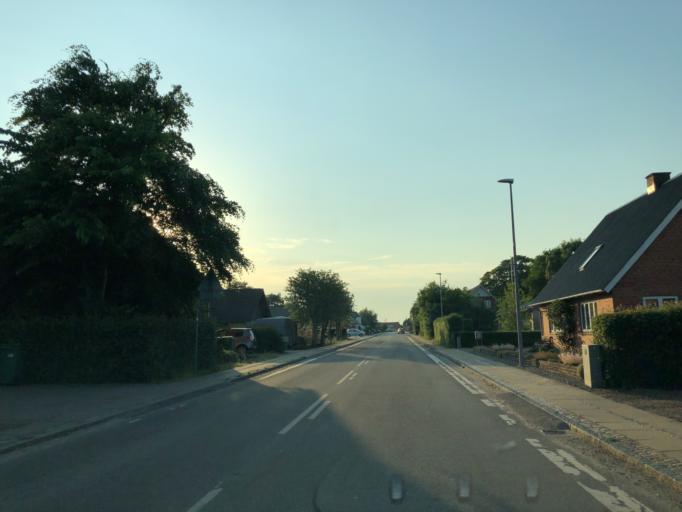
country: DK
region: Central Jutland
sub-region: Struer Kommune
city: Struer
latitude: 56.4317
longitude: 8.5160
